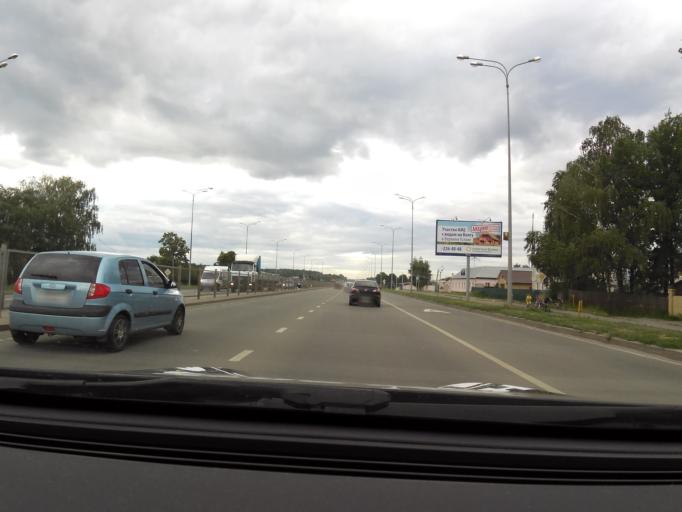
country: RU
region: Tatarstan
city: Osinovo
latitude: 55.8510
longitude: 48.8890
